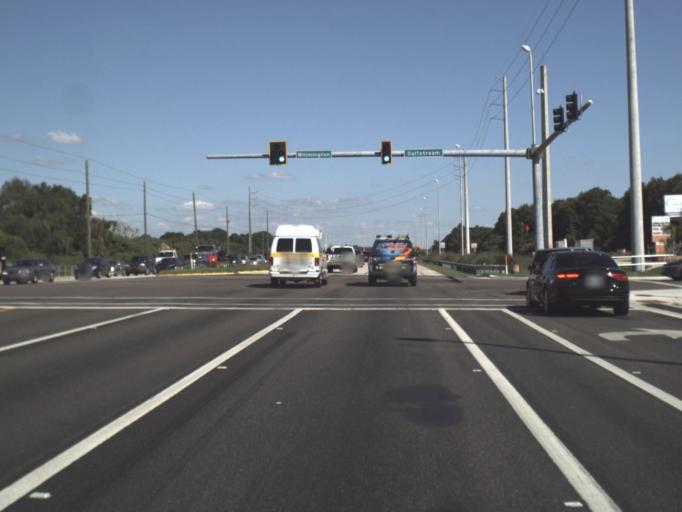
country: US
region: Florida
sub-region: Charlotte County
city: Grove City
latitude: 26.9344
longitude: -82.3022
